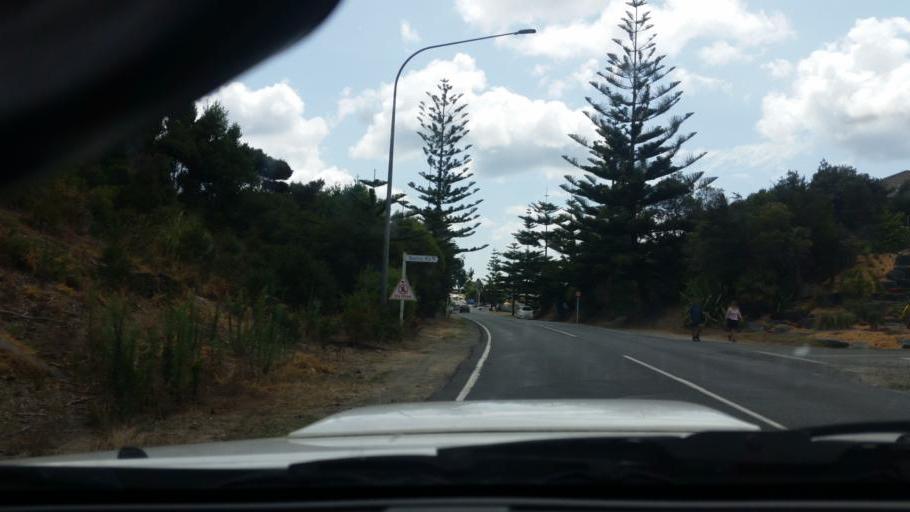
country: NZ
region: Auckland
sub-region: Auckland
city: Wellsford
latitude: -36.1039
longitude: 174.5852
